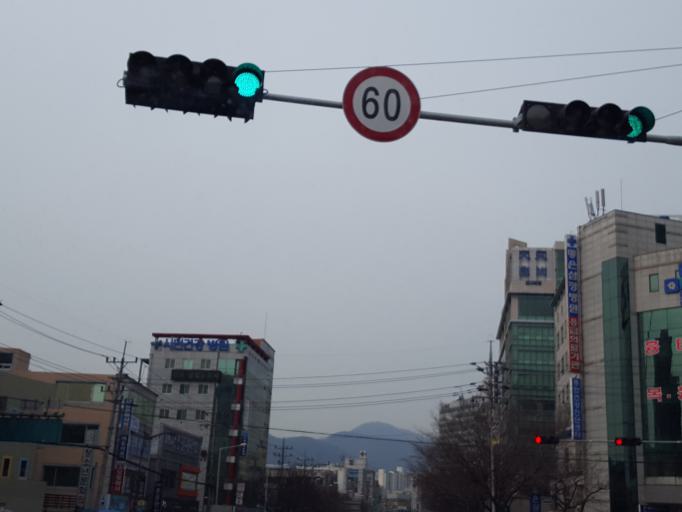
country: KR
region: Ulsan
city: Ulsan
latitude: 35.5527
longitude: 129.2694
